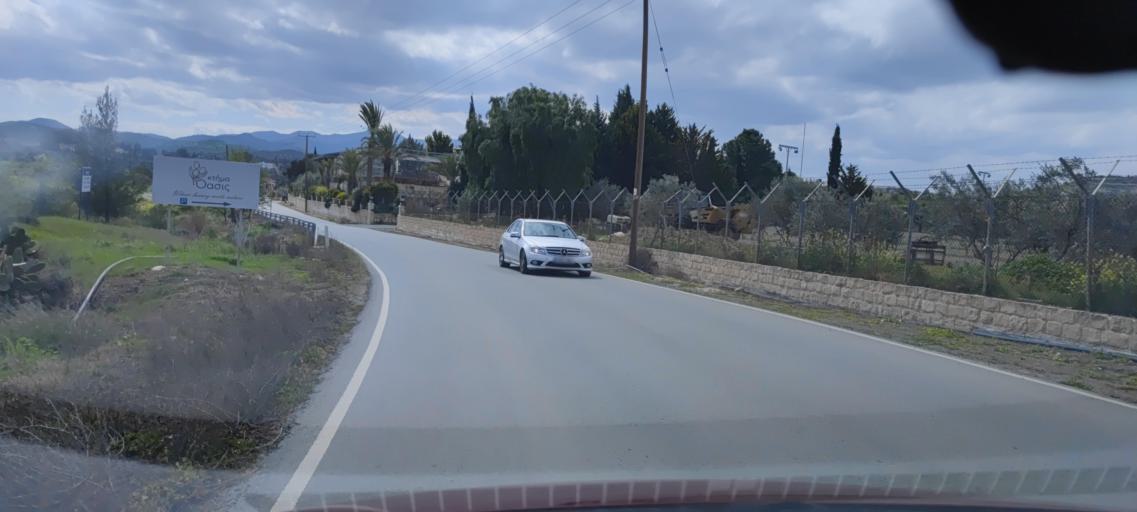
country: CY
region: Lefkosia
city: Pera
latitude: 35.0182
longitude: 33.2973
